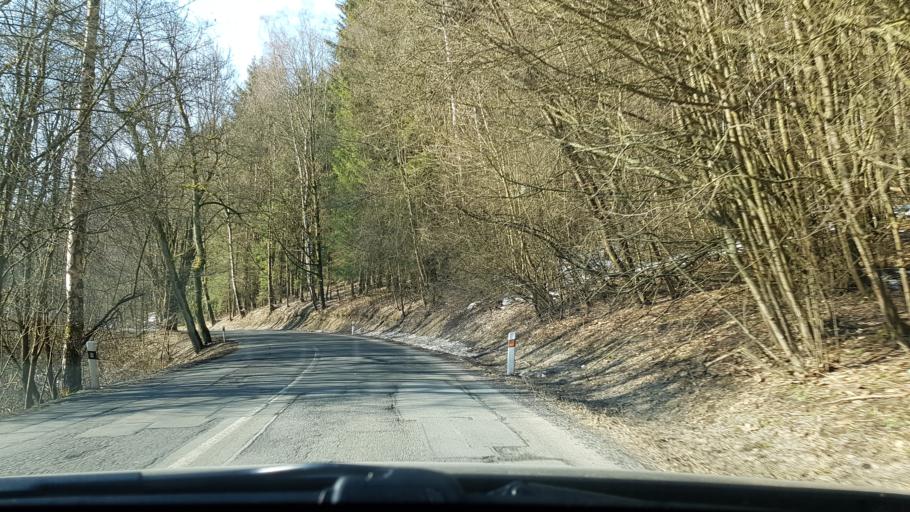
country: CZ
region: Olomoucky
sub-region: Okres Sumperk
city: Hanusovice
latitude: 50.0874
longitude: 16.9712
